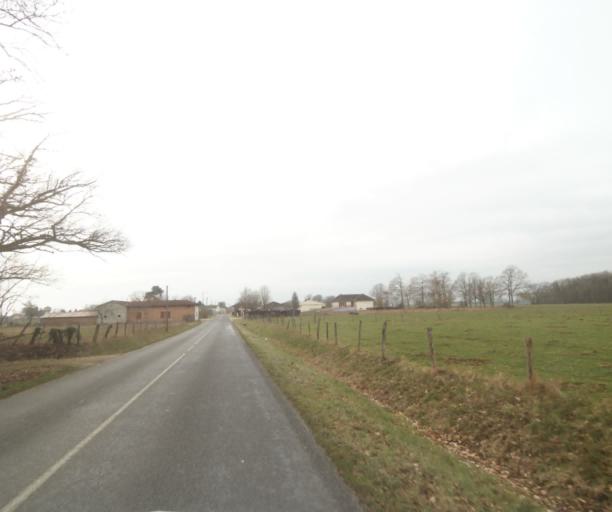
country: FR
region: Champagne-Ardenne
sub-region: Departement de la Haute-Marne
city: Villiers-en-Lieu
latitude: 48.6873
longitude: 4.8867
